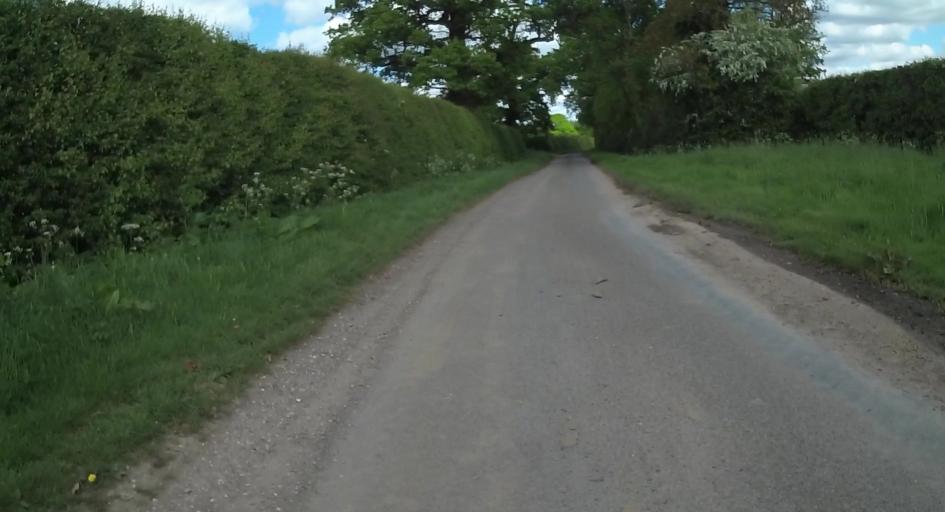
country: GB
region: England
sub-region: West Berkshire
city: Stratfield Mortimer
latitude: 51.3414
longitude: -1.0199
